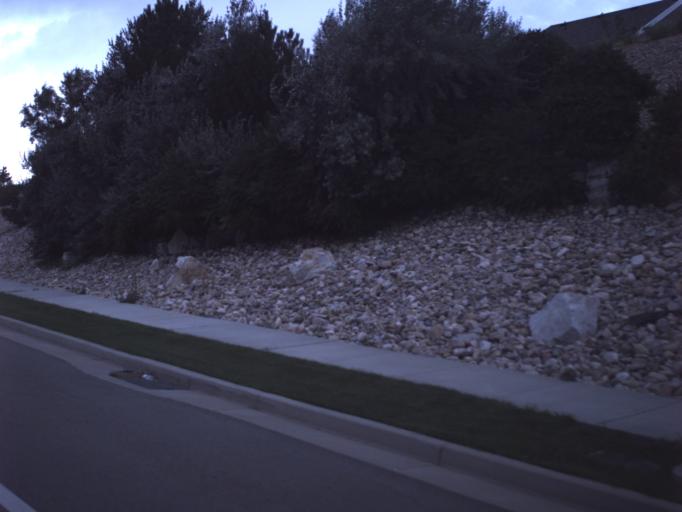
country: US
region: Utah
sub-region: Salt Lake County
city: Riverton
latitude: 40.5226
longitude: -111.9242
